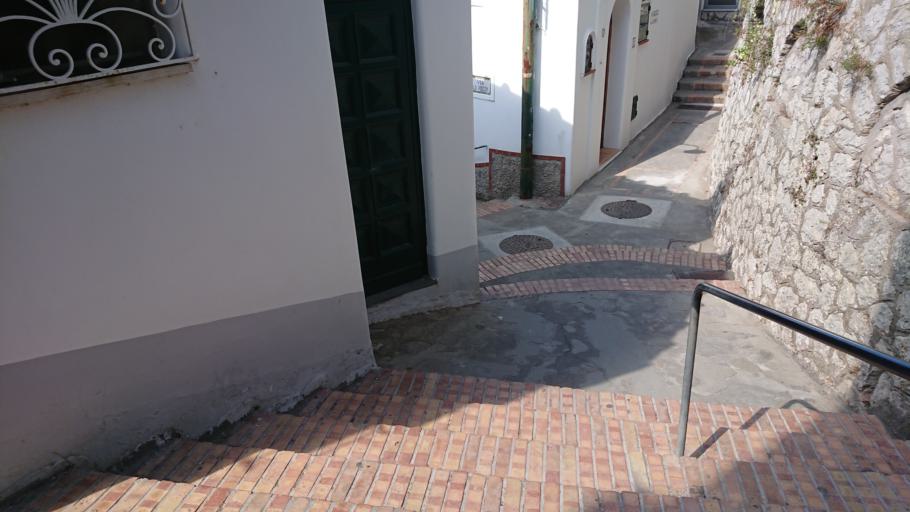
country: IT
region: Campania
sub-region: Provincia di Napoli
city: Anacapri
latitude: 40.5551
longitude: 14.2157
